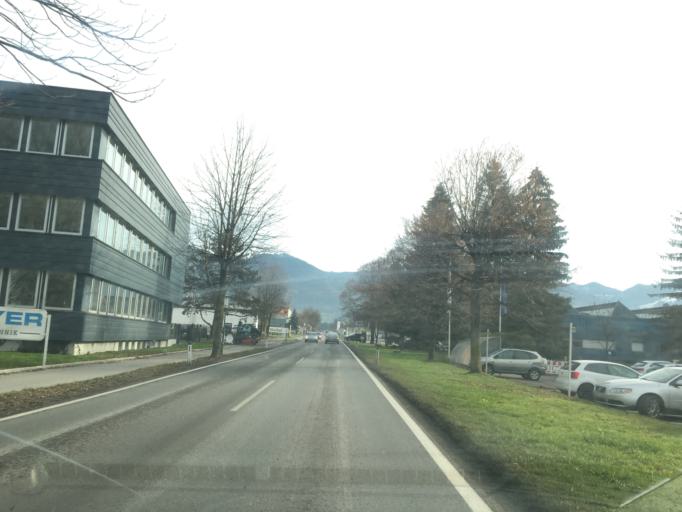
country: AT
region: Vorarlberg
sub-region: Politischer Bezirk Feldkirch
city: Klaus
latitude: 47.3074
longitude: 9.6309
